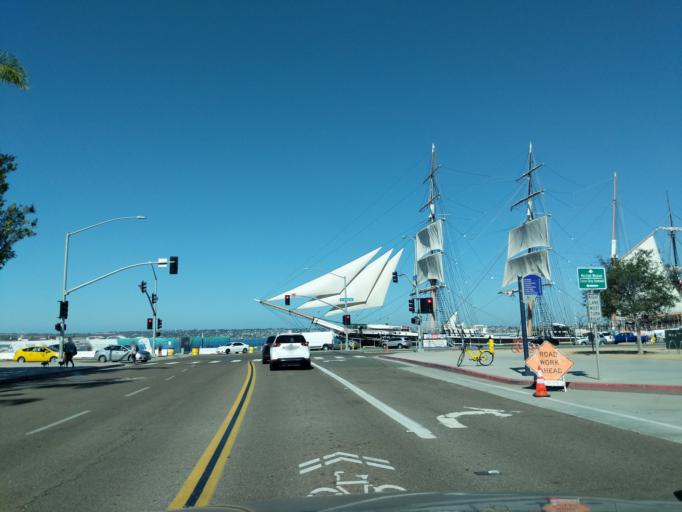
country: US
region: California
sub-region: San Diego County
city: San Diego
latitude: 32.7199
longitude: -117.1726
